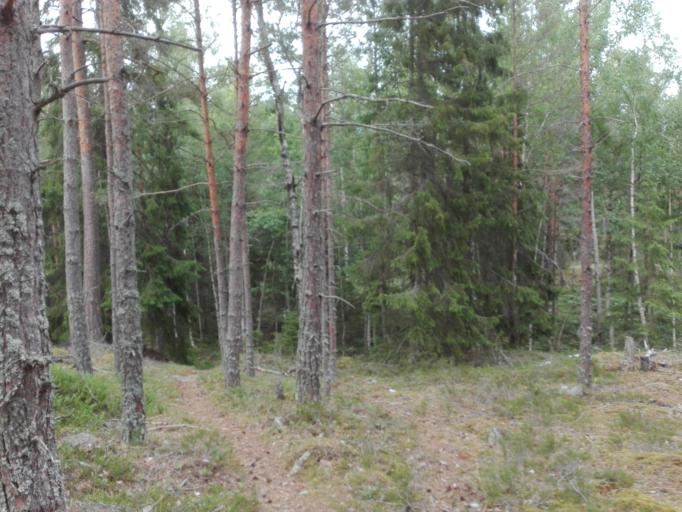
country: SE
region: Stockholm
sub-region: Nacka Kommun
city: Fisksatra
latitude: 59.2803
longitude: 18.2510
